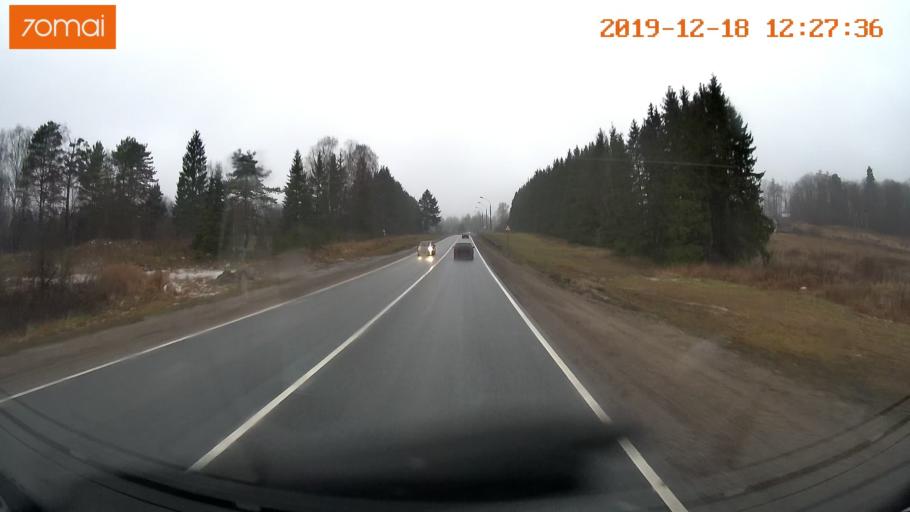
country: RU
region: Moskovskaya
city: Novopetrovskoye
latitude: 56.0646
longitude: 36.5019
